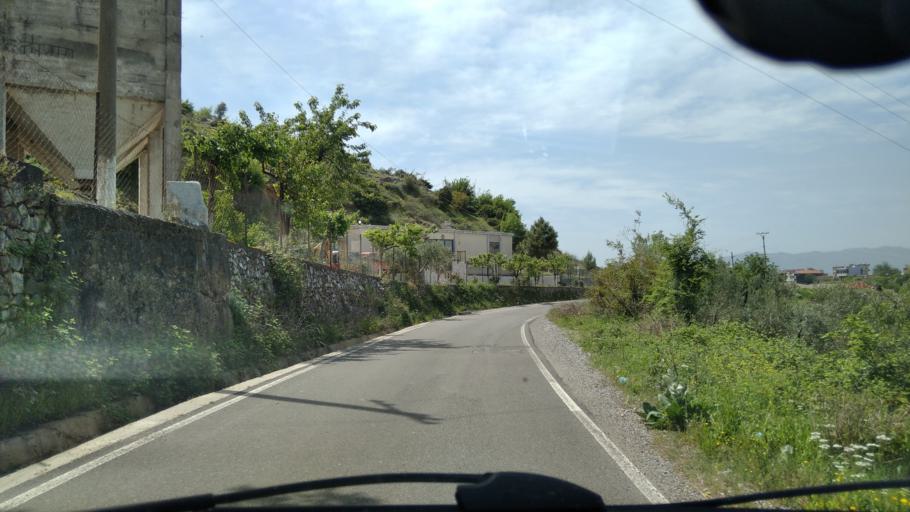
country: AL
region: Shkoder
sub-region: Rrethi i Shkodres
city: Guri i Zi
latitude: 42.1166
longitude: 19.5791
